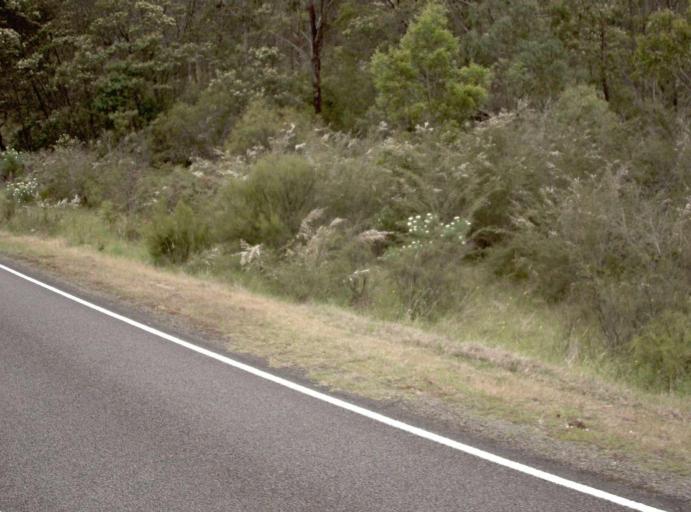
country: AU
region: New South Wales
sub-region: Bombala
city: Bombala
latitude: -37.2333
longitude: 149.2709
